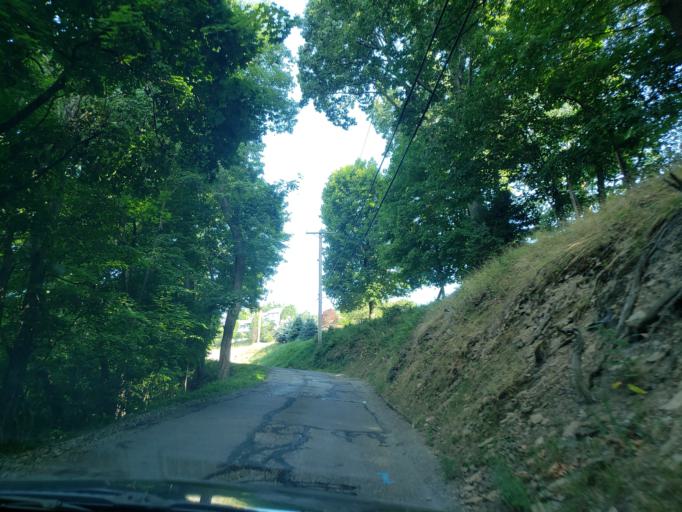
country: US
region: Pennsylvania
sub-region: Allegheny County
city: Coraopolis
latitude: 40.5306
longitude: -80.1601
